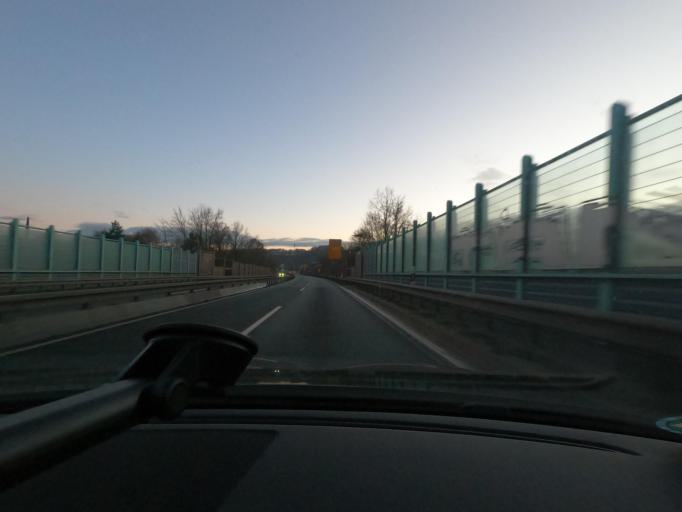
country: DE
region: Lower Saxony
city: Osterode am Harz
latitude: 51.7404
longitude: 10.2301
